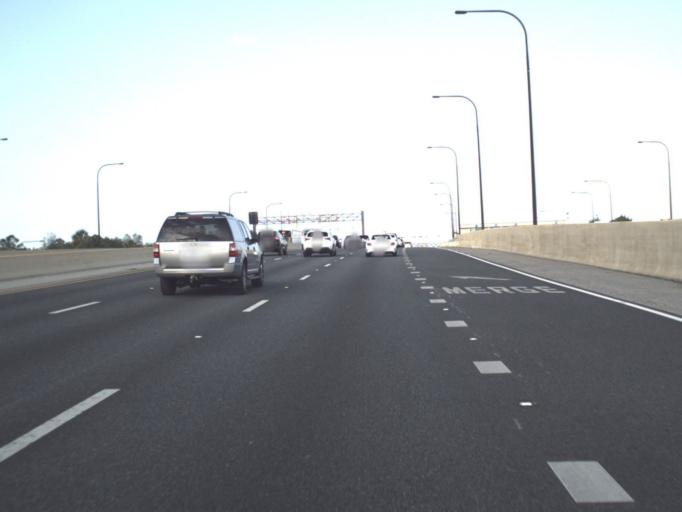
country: US
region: Florida
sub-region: Orange County
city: Azalea Park
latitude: 28.5396
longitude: -81.3211
